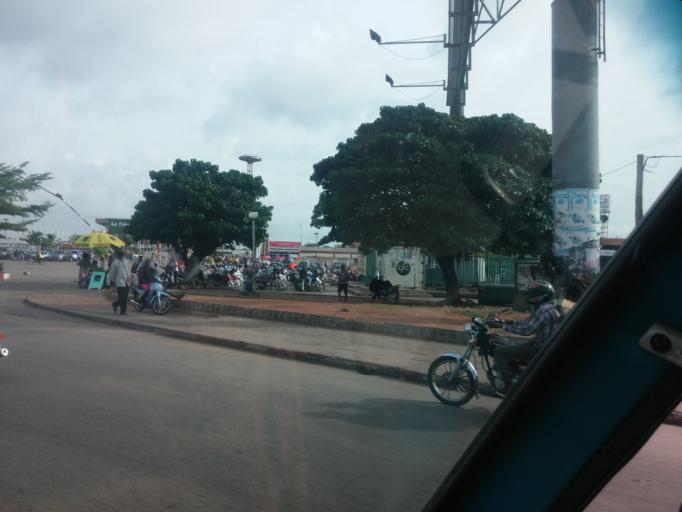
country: BJ
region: Littoral
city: Cotonou
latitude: 6.3836
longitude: 2.3783
